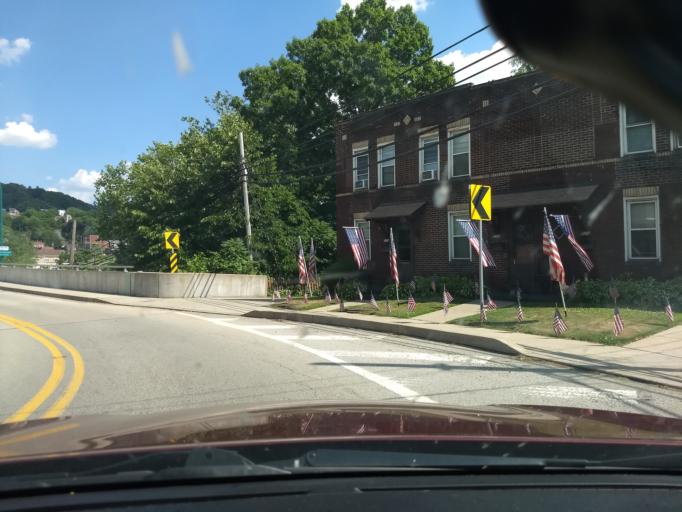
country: US
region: Pennsylvania
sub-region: Westmoreland County
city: Trafford
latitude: 40.3866
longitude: -79.7647
